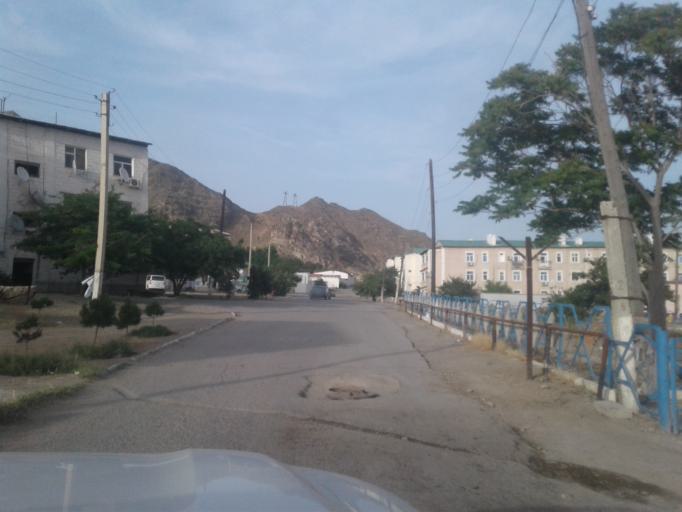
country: TM
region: Balkan
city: Turkmenbasy
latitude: 40.0016
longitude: 52.9742
